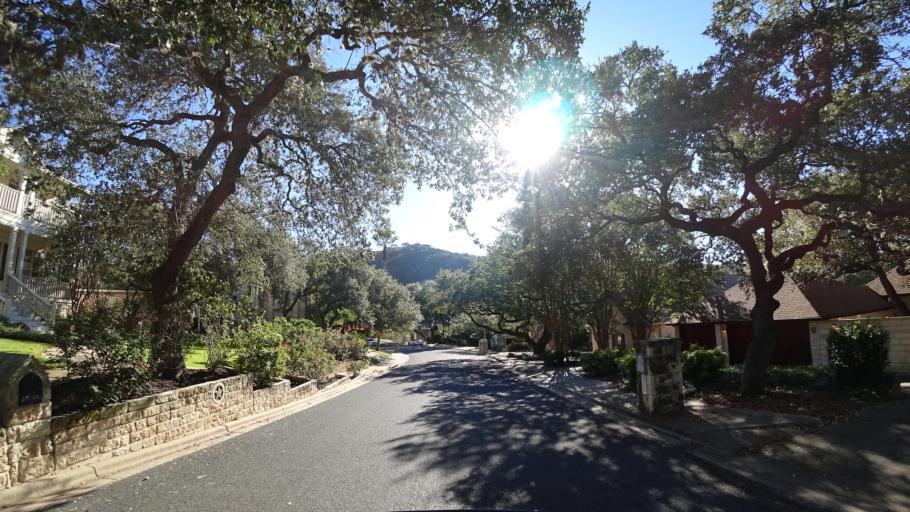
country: US
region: Texas
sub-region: Travis County
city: West Lake Hills
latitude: 30.3535
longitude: -97.7871
